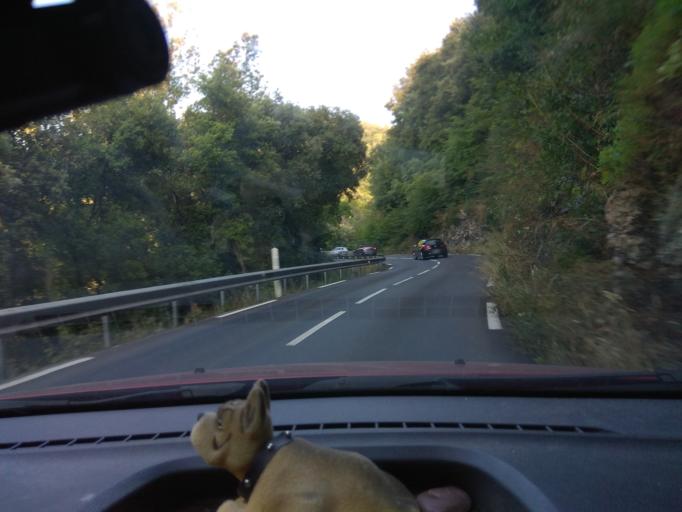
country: FR
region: Provence-Alpes-Cote d'Azur
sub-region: Departement des Alpes-Maritimes
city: La Colle-sur-Loup
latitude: 43.6882
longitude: 7.0691
